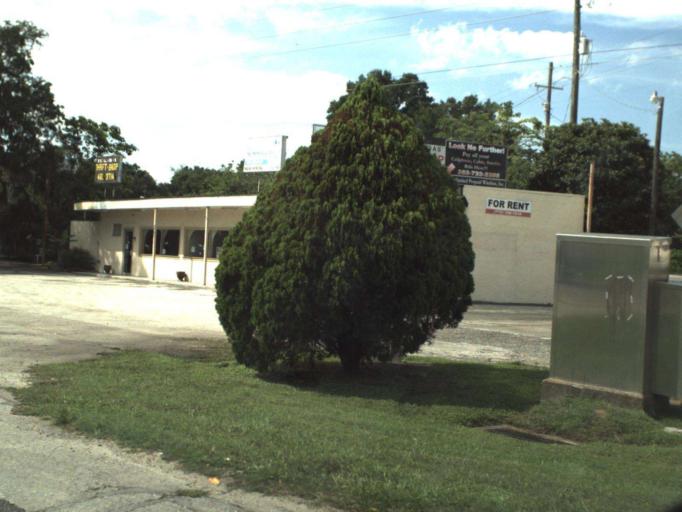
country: US
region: Florida
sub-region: Marion County
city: Ocala
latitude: 29.1476
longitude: -82.1153
